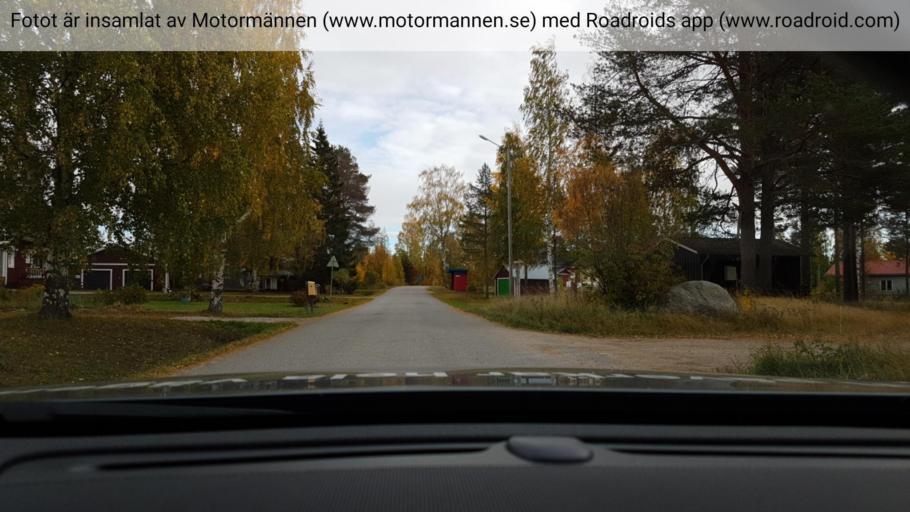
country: SE
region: Norrbotten
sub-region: Overkalix Kommun
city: OEverkalix
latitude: 66.3062
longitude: 22.9164
